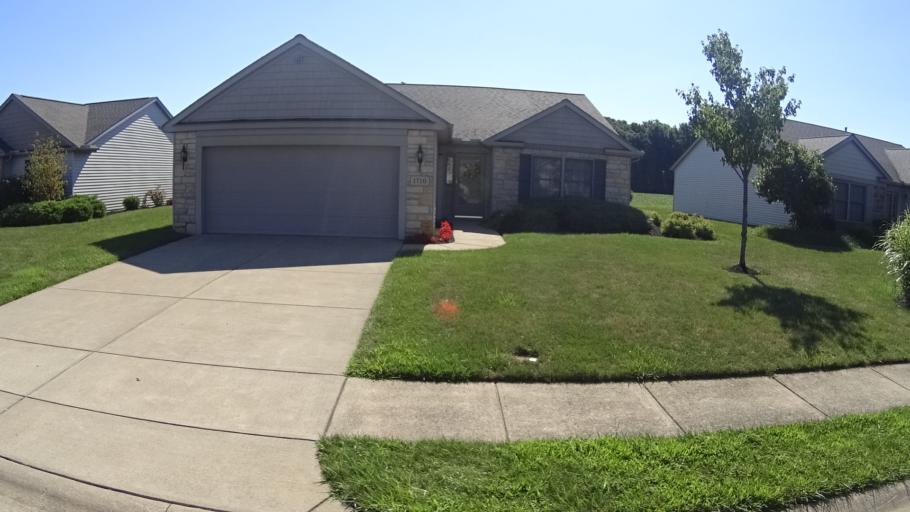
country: US
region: Ohio
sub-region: Erie County
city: Huron
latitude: 41.3940
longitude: -82.6408
